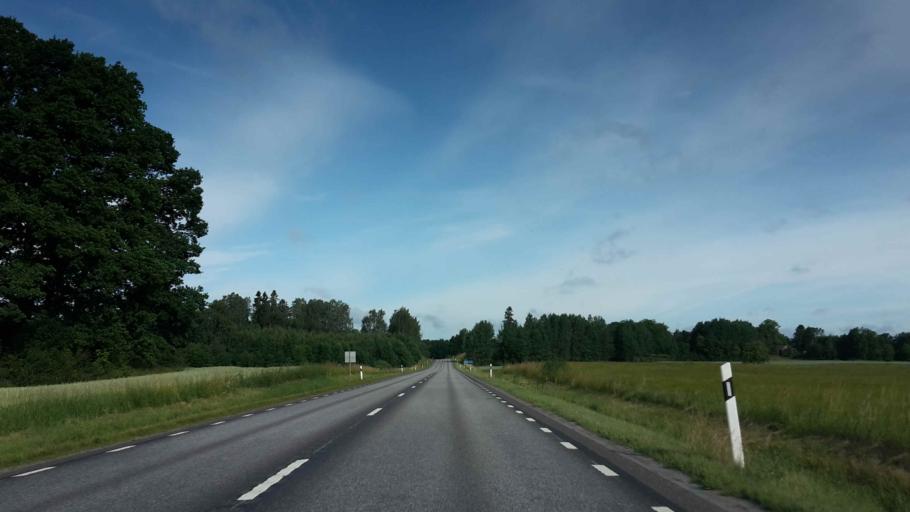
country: SE
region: OEstergoetland
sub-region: Motala Kommun
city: Borensberg
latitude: 58.5336
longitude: 15.3890
